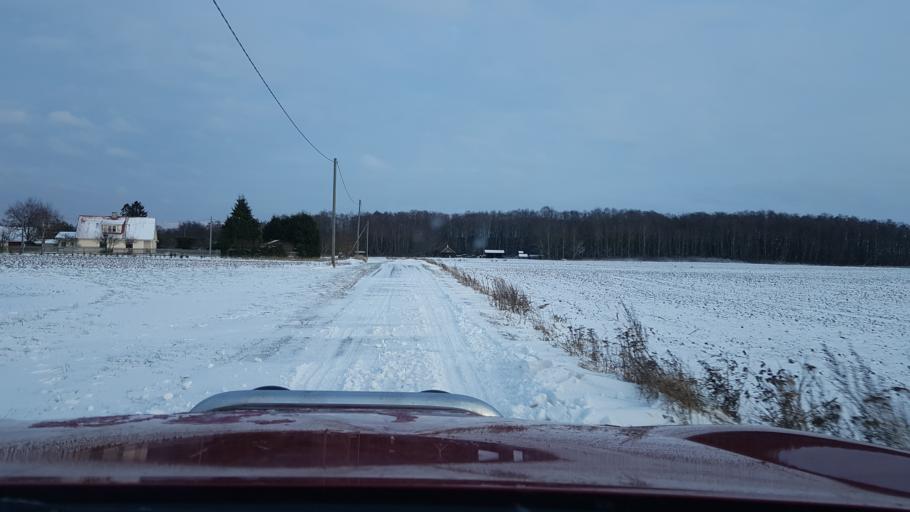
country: EE
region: Harju
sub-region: Maardu linn
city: Maardu
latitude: 59.4294
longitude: 25.0417
